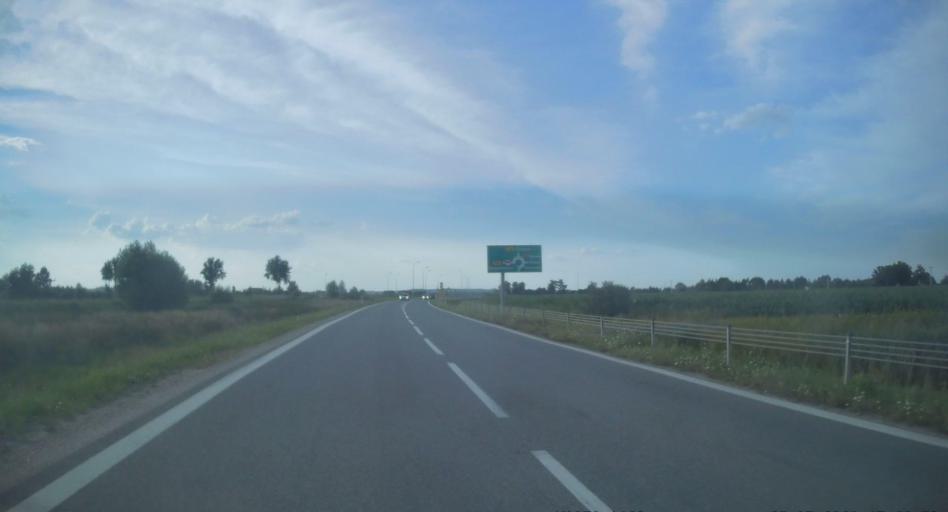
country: PL
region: Lesser Poland Voivodeship
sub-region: Powiat brzeski
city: Szczurowa
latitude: 50.1203
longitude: 20.6136
